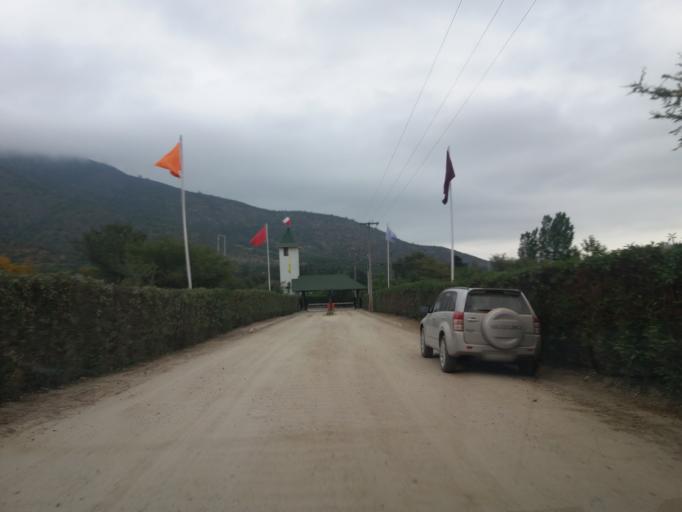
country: CL
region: Valparaiso
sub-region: Provincia de Marga Marga
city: Limache
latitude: -33.0284
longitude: -71.1423
